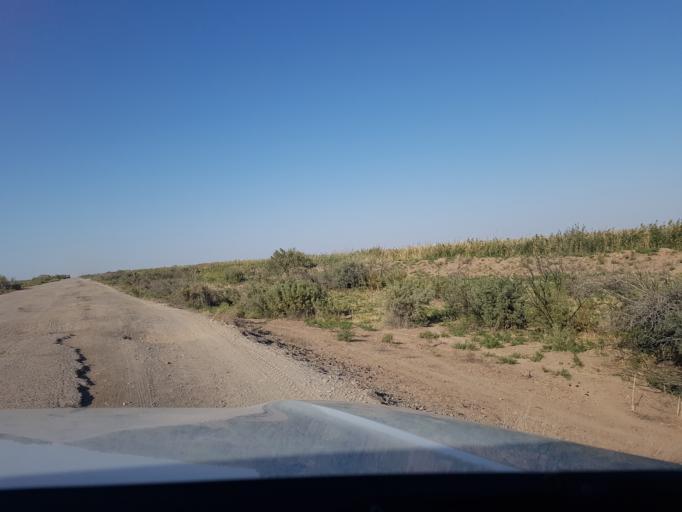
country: IR
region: Razavi Khorasan
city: Sarakhs
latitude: 36.9523
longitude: 61.3803
